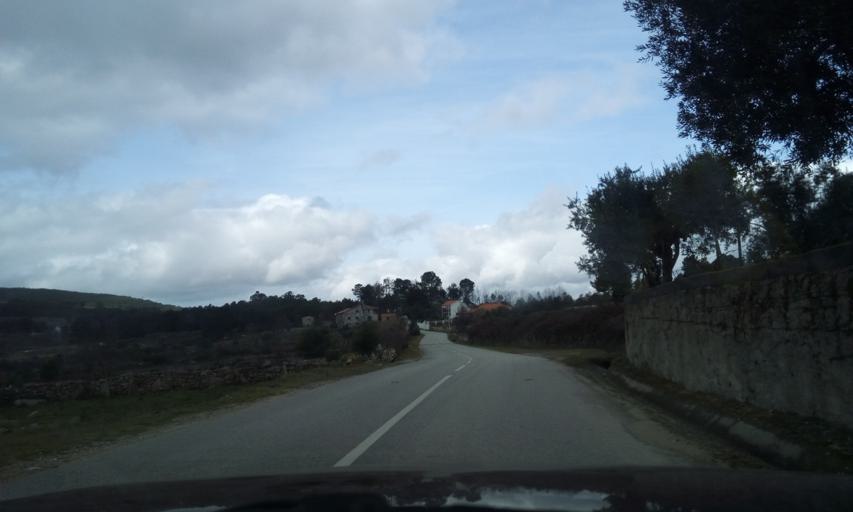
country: PT
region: Guarda
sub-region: Fornos de Algodres
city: Fornos de Algodres
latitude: 40.6606
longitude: -7.5958
